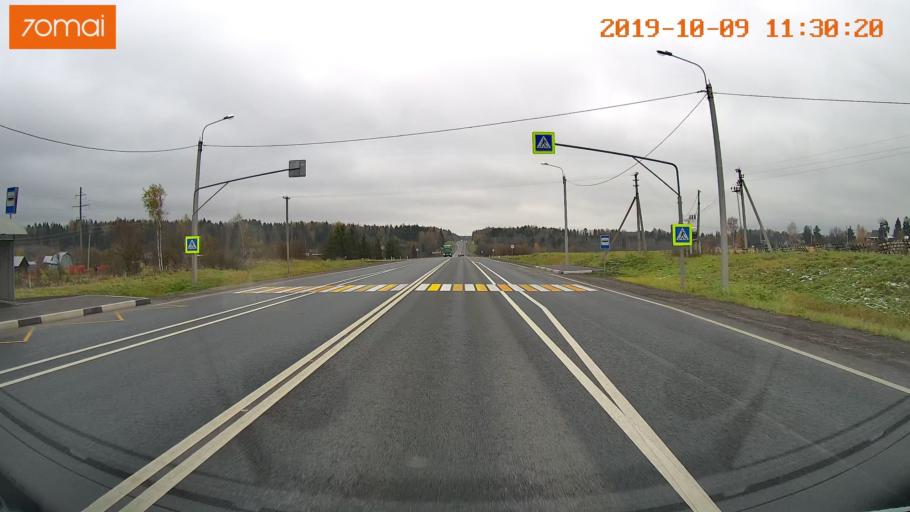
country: RU
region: Vologda
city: Gryazovets
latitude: 59.0547
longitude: 40.0730
